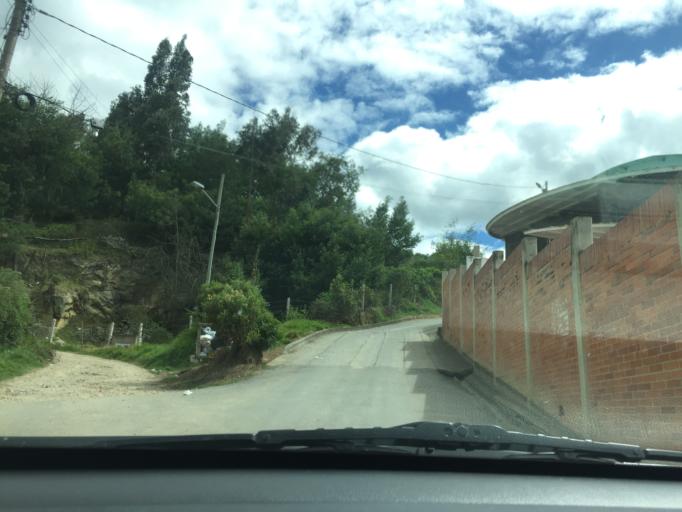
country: CO
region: Cundinamarca
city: Tocancipa
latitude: 4.9679
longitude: -73.8993
